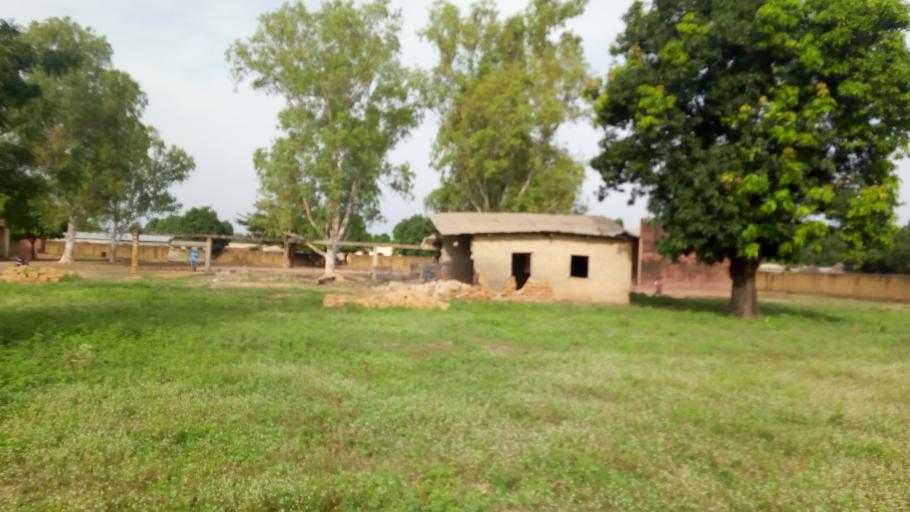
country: ML
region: Koulikoro
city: Kangaba
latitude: 11.6426
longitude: -8.7513
